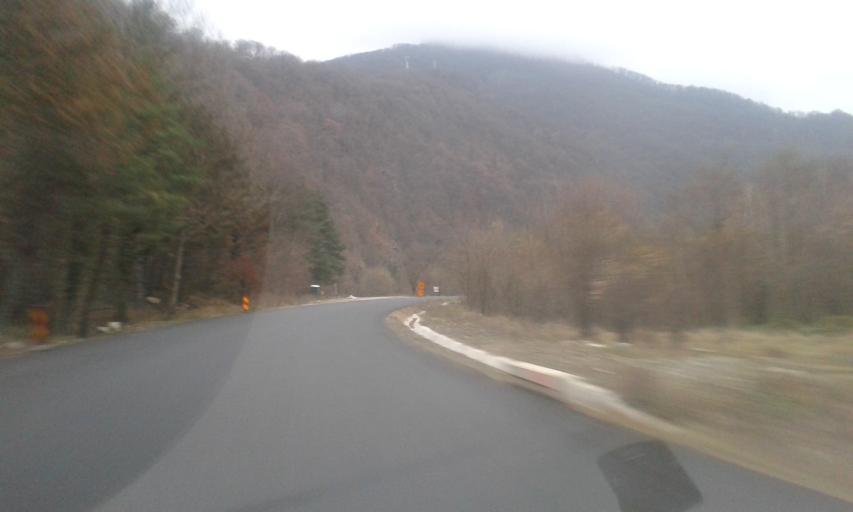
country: RO
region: Gorj
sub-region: Comuna Bumbesti-Jiu
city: Bumbesti-Jiu
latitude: 45.2709
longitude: 23.3803
